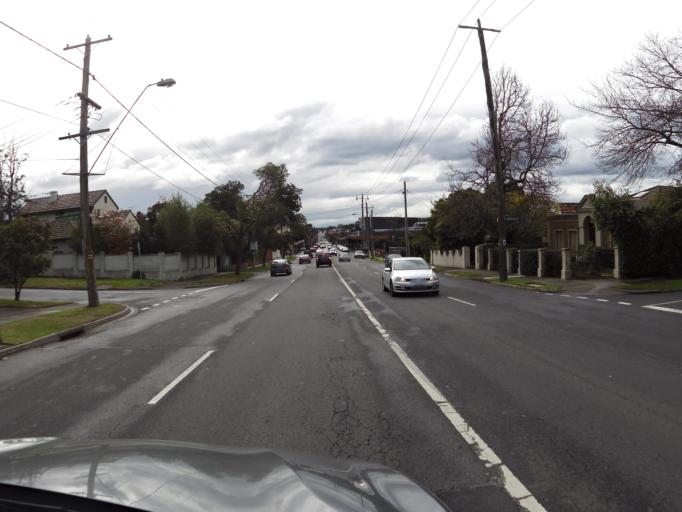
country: AU
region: Victoria
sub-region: Boroondara
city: Kew East
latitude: -37.8030
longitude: 145.0621
